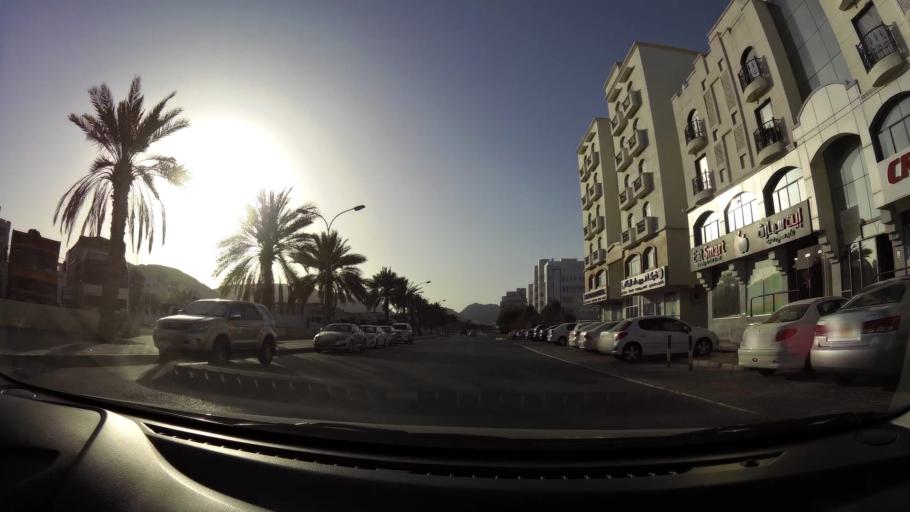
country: OM
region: Muhafazat Masqat
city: Muscat
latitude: 23.5898
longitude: 58.5521
